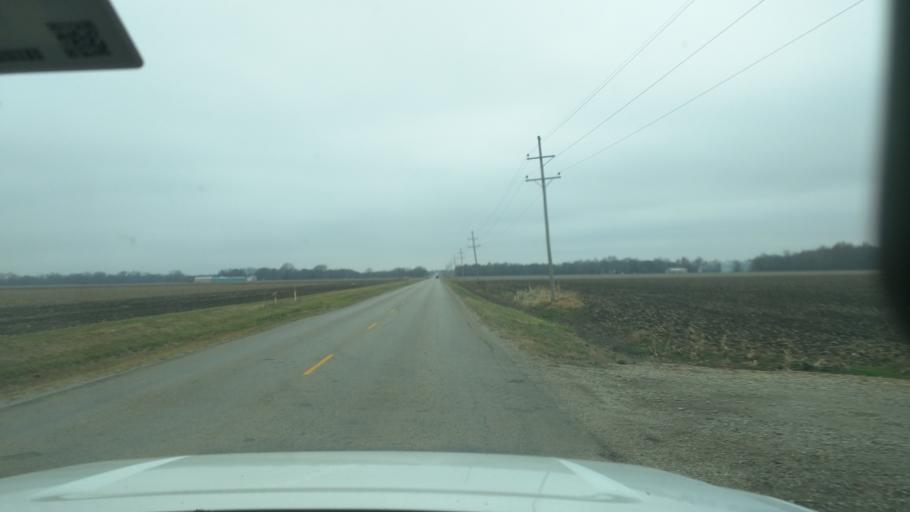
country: US
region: Kansas
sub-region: Lyon County
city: Emporia
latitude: 38.4811
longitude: -96.2530
